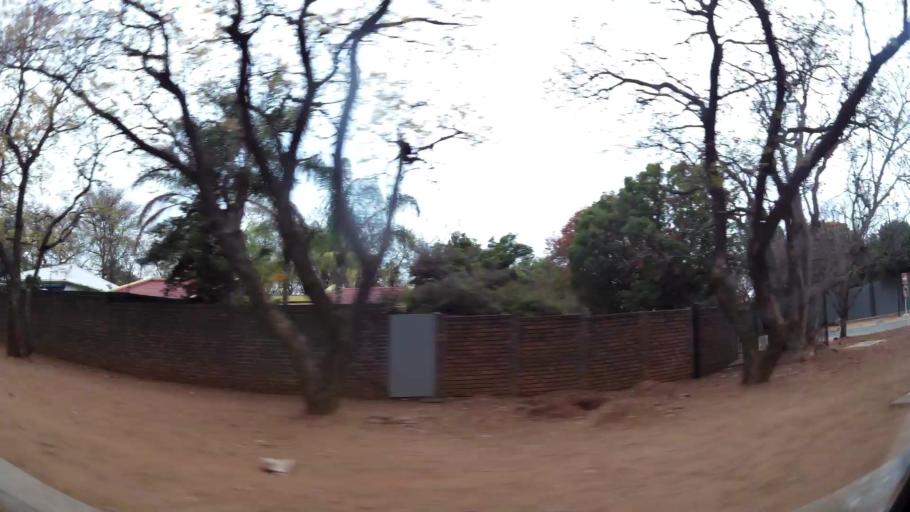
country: ZA
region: Limpopo
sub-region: Capricorn District Municipality
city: Polokwane
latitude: -23.9017
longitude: 29.4671
